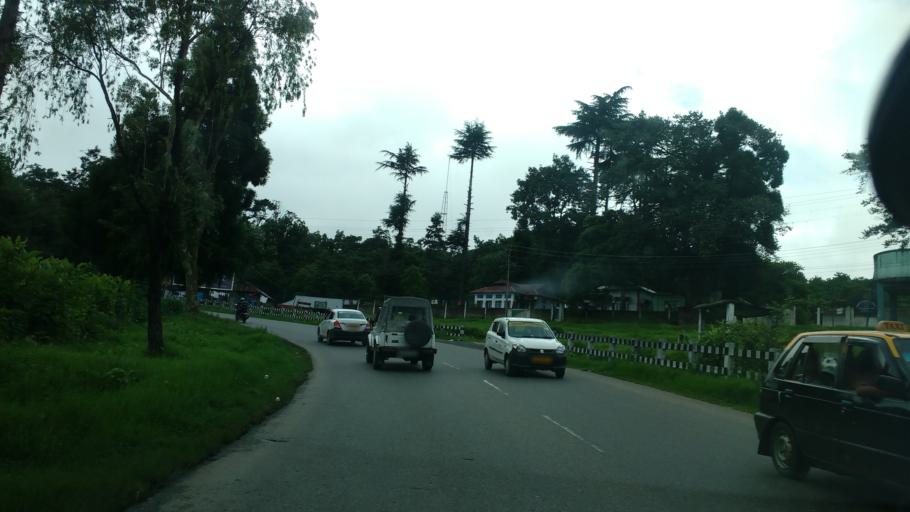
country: IN
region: Meghalaya
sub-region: East Khasi Hills
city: Shillong
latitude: 25.5498
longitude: 91.8417
